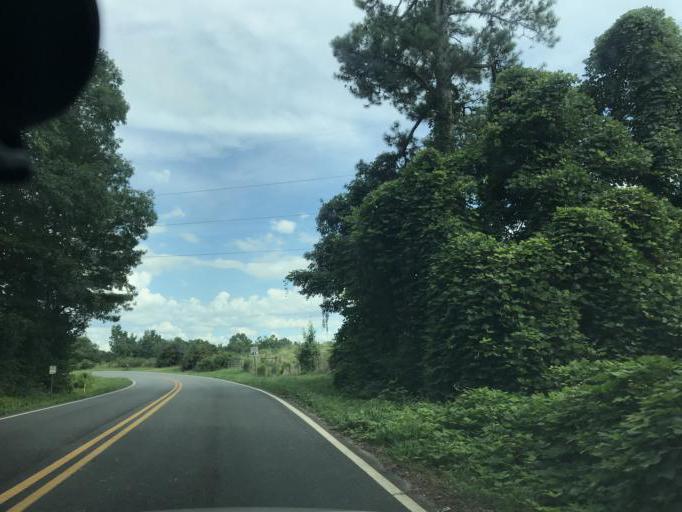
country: US
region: Georgia
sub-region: Cherokee County
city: Ball Ground
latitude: 34.3283
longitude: -84.2572
